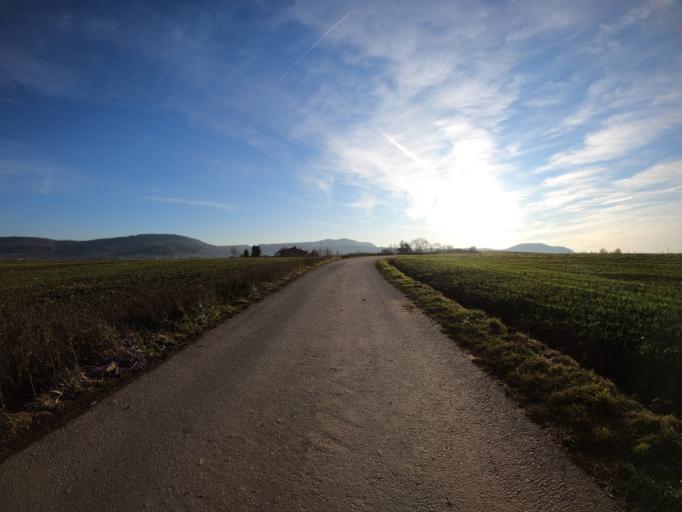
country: DE
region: Baden-Wuerttemberg
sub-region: Regierungsbezirk Stuttgart
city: Boll
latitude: 48.6554
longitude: 9.6082
